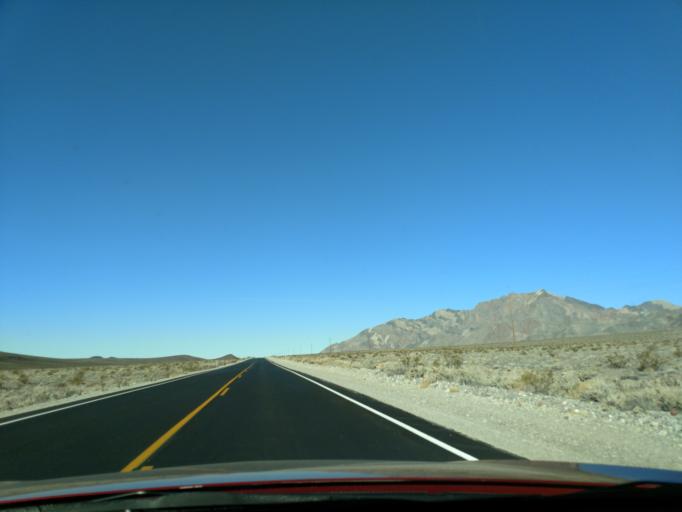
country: US
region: Nevada
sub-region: Nye County
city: Pahrump
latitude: 36.3238
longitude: -116.5606
